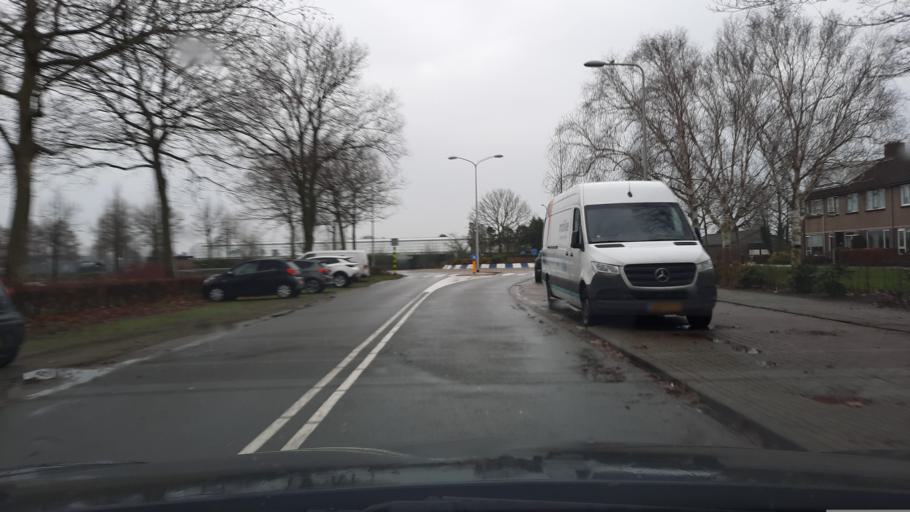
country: NL
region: South Holland
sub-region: Gemeente Noordwijkerhout
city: Noordwijkerhout
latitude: 52.2576
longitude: 4.4988
